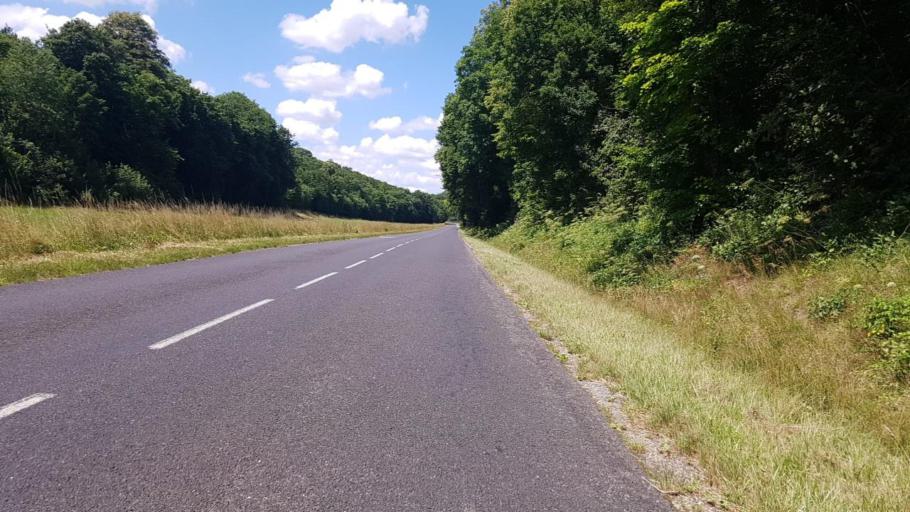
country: FR
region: Lorraine
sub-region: Departement de la Meuse
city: Vacon
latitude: 48.6711
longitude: 5.5665
